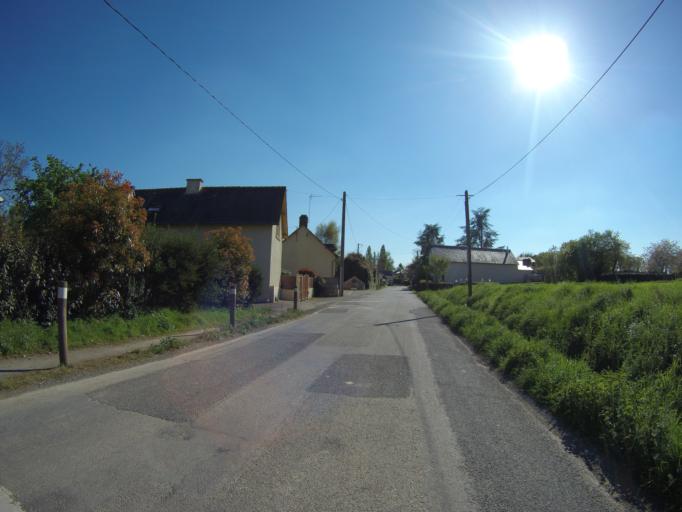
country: FR
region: Brittany
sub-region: Departement d'Ille-et-Vilaine
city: Vern-sur-Seiche
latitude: 48.0498
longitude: -1.6184
